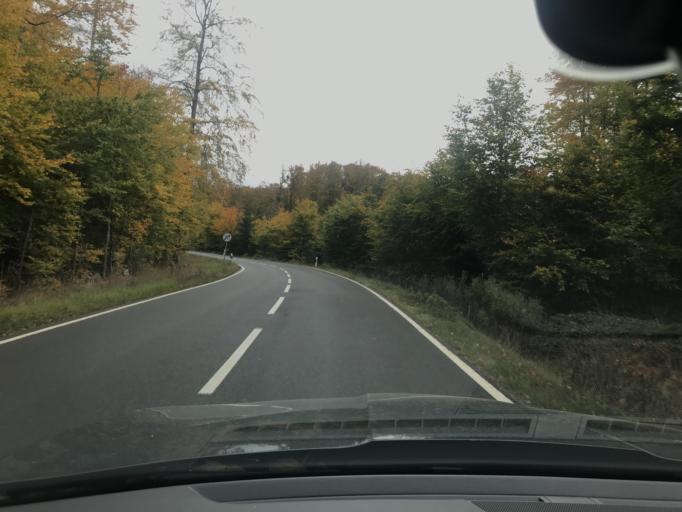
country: DE
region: Saxony-Anhalt
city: Friedrichsbrunn
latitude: 51.7032
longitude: 11.0267
